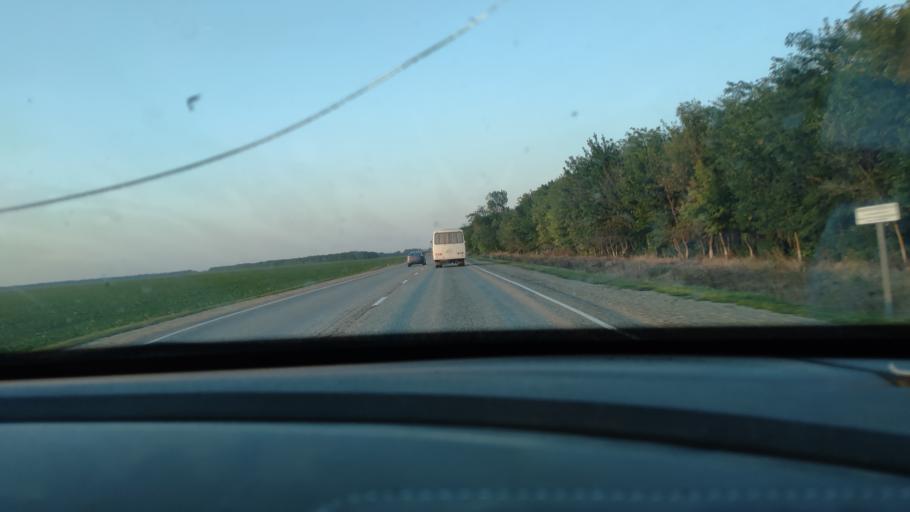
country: RU
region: Krasnodarskiy
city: Starominskaya
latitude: 46.4528
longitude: 39.0314
